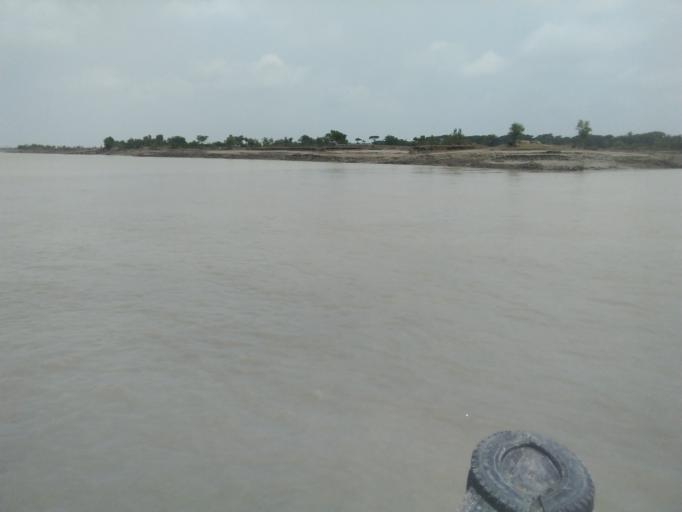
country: BD
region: Khulna
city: Phultala
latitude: 22.6449
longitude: 89.4109
